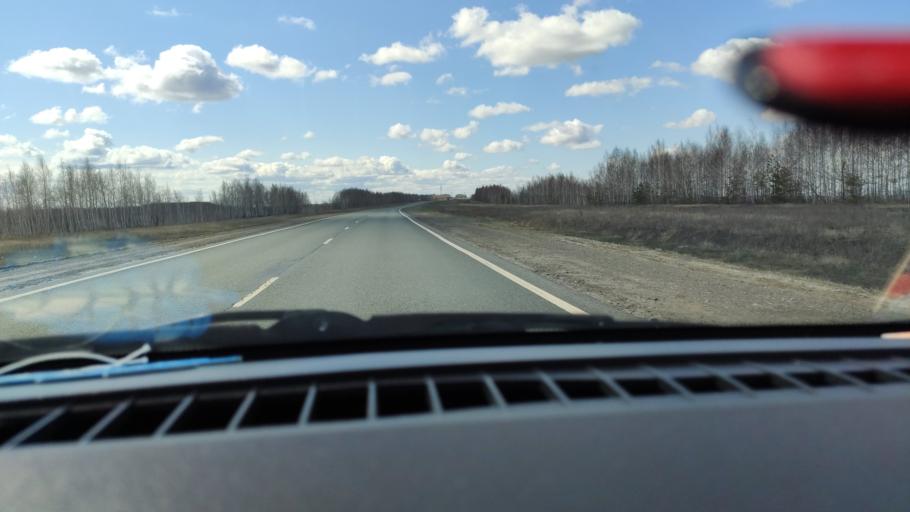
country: RU
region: Saratov
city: Dukhovnitskoye
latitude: 52.8465
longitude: 48.2531
